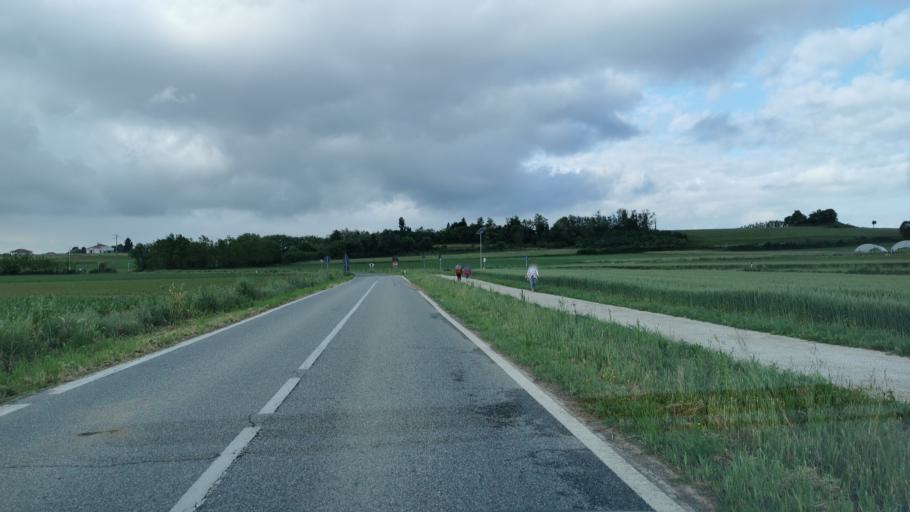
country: IT
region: Piedmont
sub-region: Provincia di Torino
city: Cambiano
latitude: 44.9876
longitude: 7.7809
